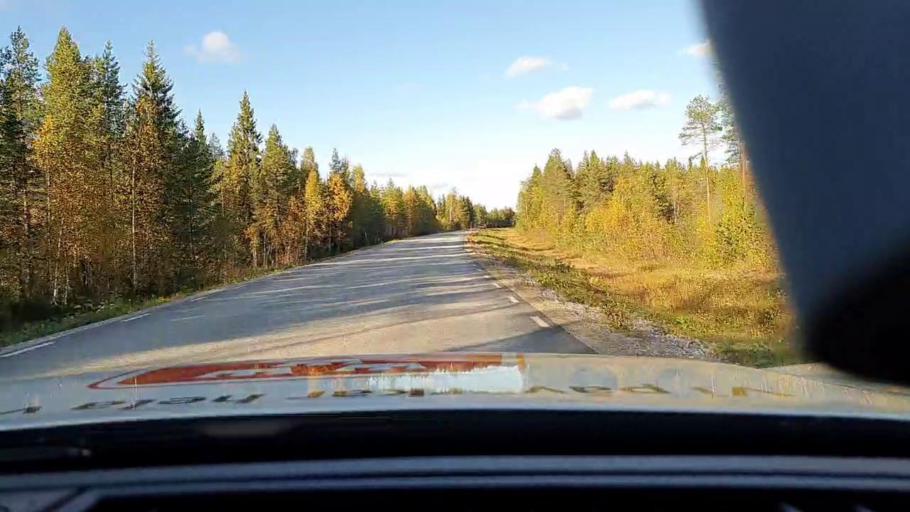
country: SE
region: Norrbotten
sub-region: Pitea Kommun
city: Norrfjarden
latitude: 65.5003
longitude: 21.4759
